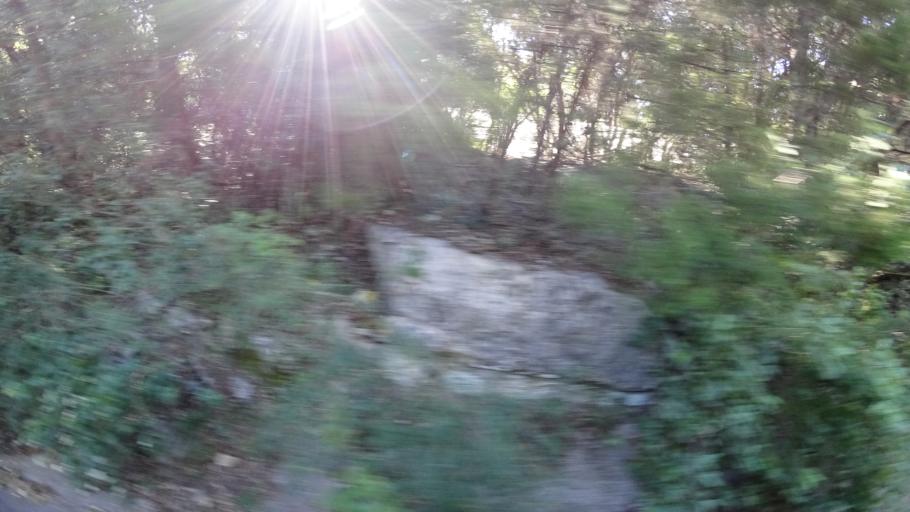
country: US
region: Texas
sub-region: Travis County
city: West Lake Hills
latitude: 30.3408
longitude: -97.7920
